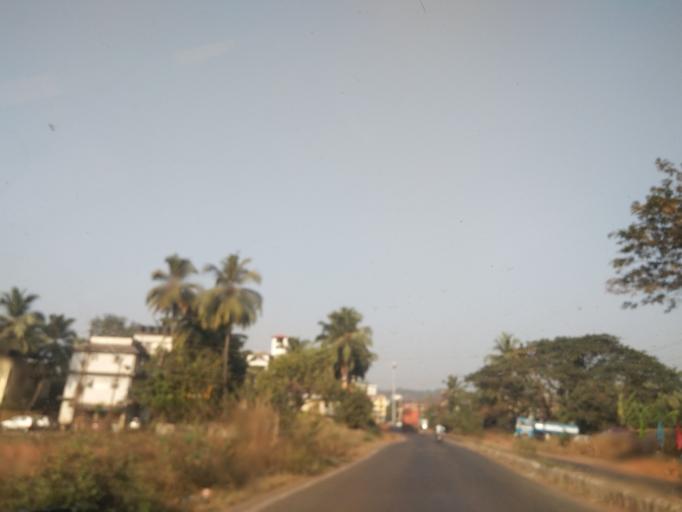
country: IN
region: Goa
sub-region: South Goa
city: Davorlim
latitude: 15.2713
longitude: 73.9808
